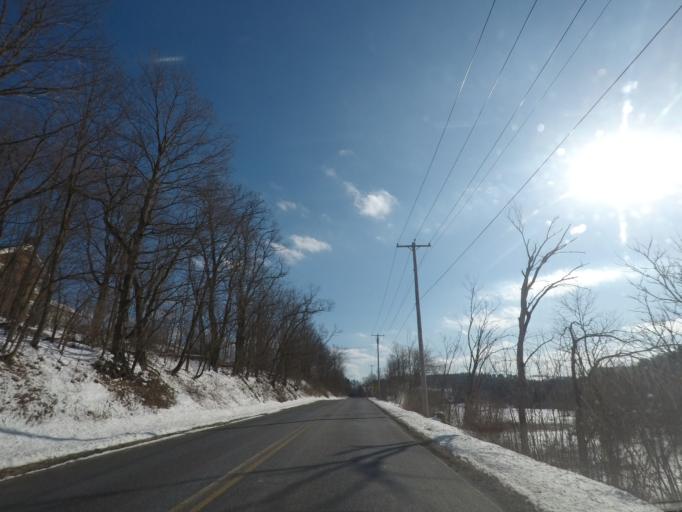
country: US
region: New York
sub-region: Rensselaer County
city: Hoosick Falls
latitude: 42.8784
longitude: -73.4988
